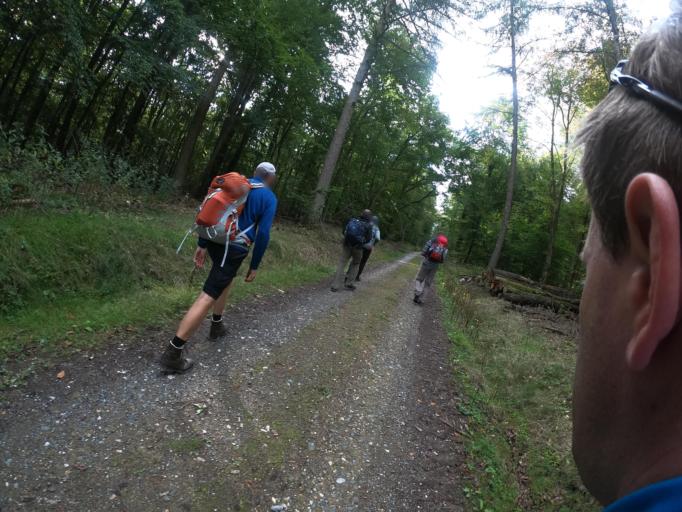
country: DE
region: Hesse
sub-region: Regierungsbezirk Darmstadt
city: Idstein
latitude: 50.2328
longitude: 8.2413
